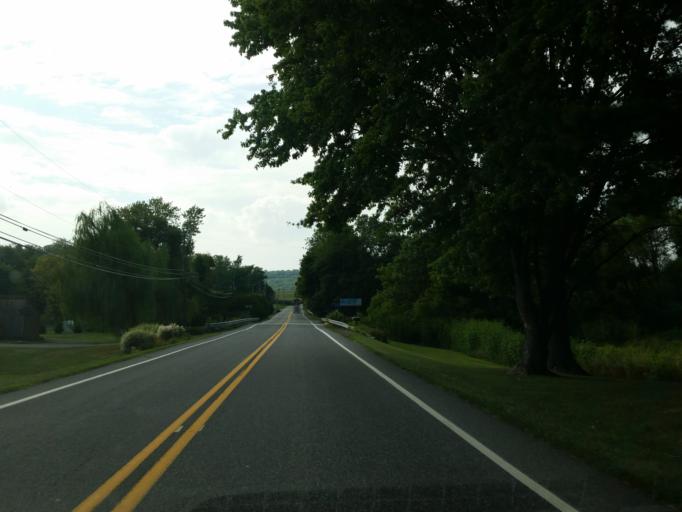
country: US
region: Pennsylvania
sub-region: Lancaster County
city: Mount Joy
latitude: 40.2067
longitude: -76.5011
